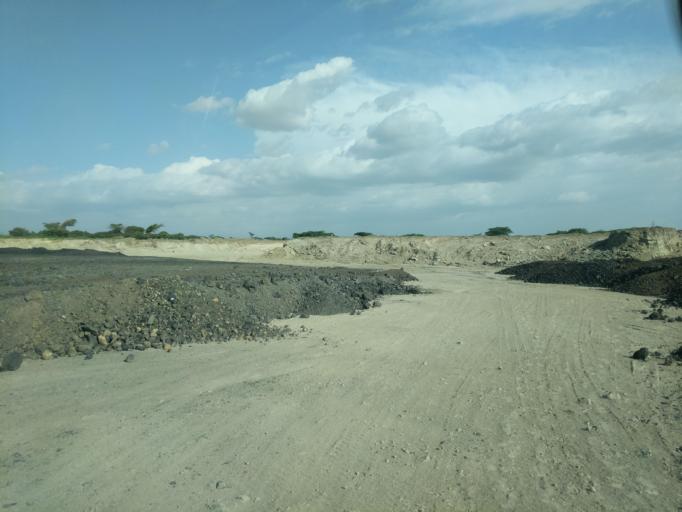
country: ET
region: Oromiya
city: Ziway
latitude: 7.5814
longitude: 38.6821
